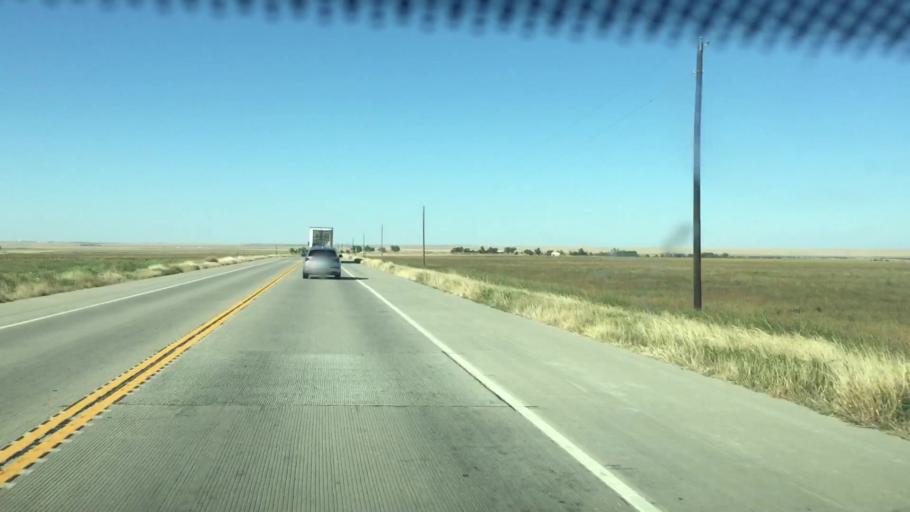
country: US
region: Colorado
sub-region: Kiowa County
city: Eads
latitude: 38.3184
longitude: -102.7199
